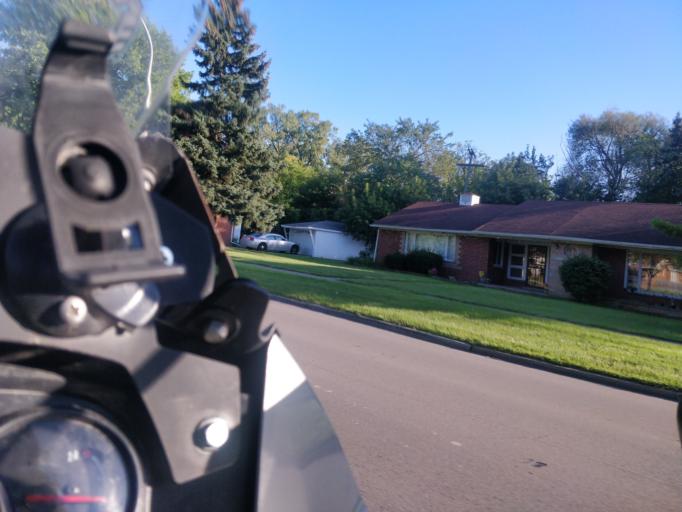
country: US
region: Michigan
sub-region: Wayne County
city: Melvindale
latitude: 42.2712
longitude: -83.1901
